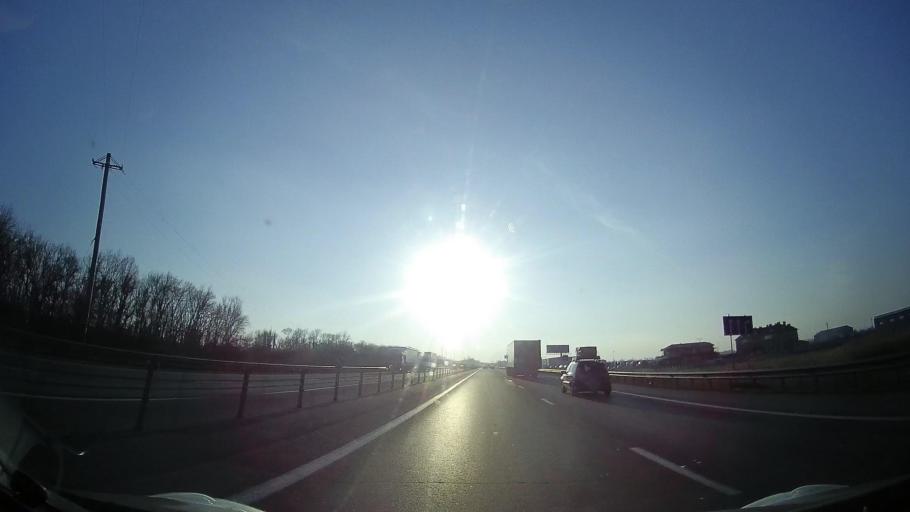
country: RU
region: Rostov
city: Ol'ginskaya
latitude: 47.1237
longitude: 39.8689
